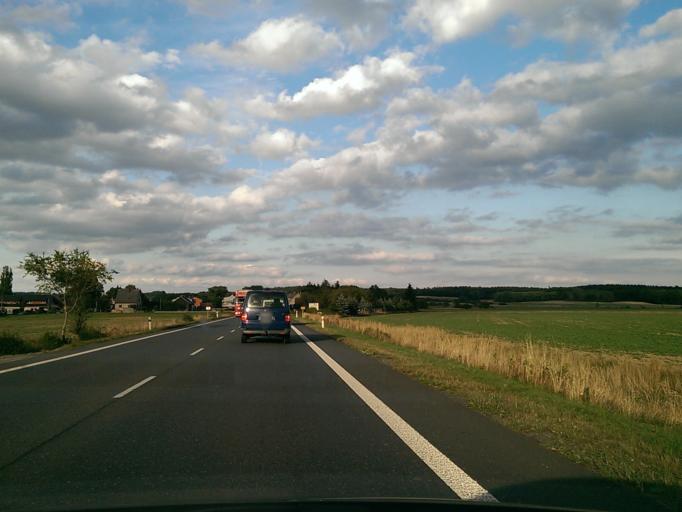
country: CZ
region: Central Bohemia
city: Knezmost
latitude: 50.4428
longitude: 15.0622
